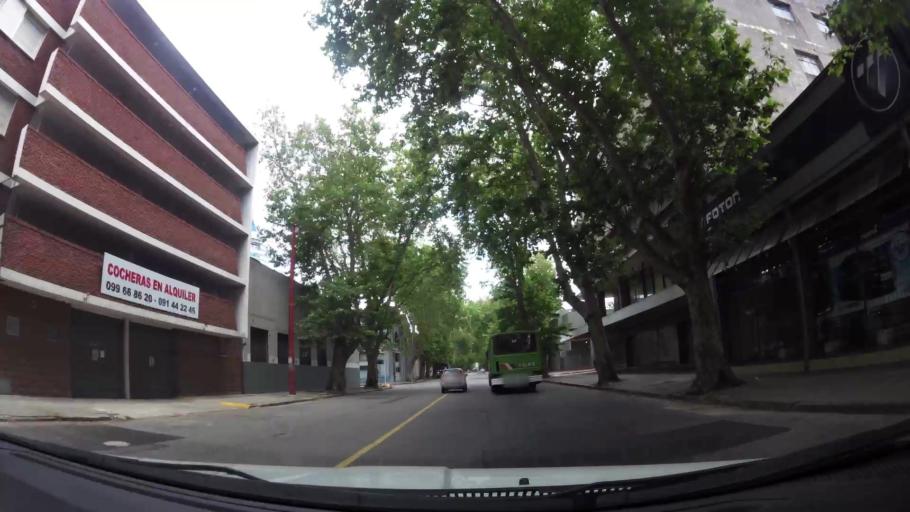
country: UY
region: Montevideo
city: Montevideo
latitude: -34.8945
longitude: -56.1926
